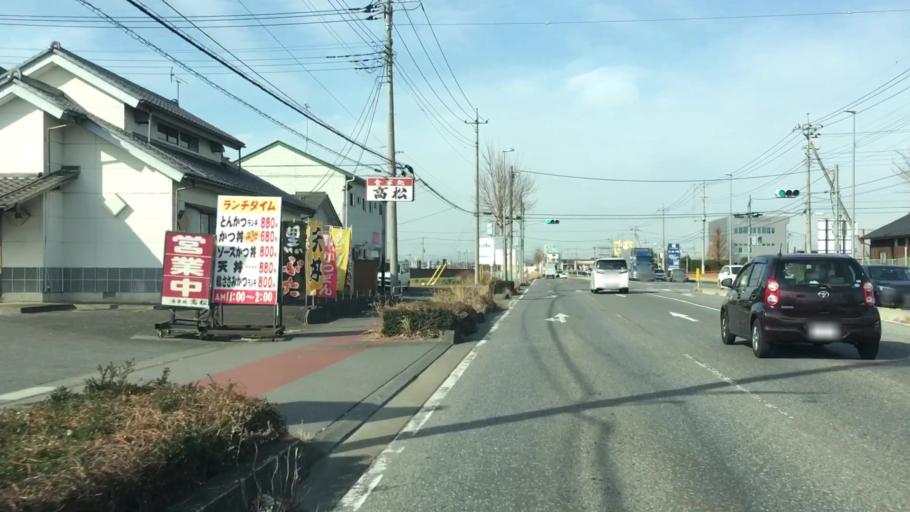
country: JP
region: Gunma
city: Tatebayashi
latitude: 36.2353
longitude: 139.4789
